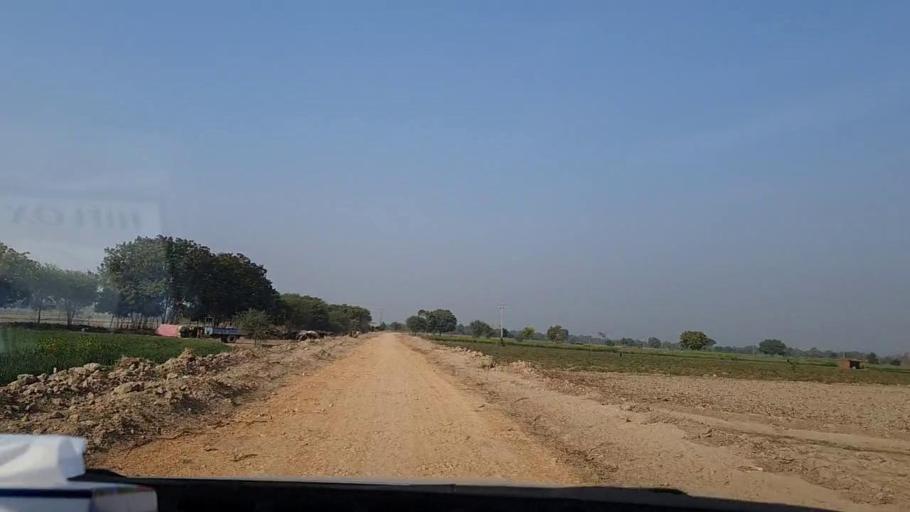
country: PK
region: Sindh
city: Tando Ghulam Ali
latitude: 25.1853
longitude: 68.8747
